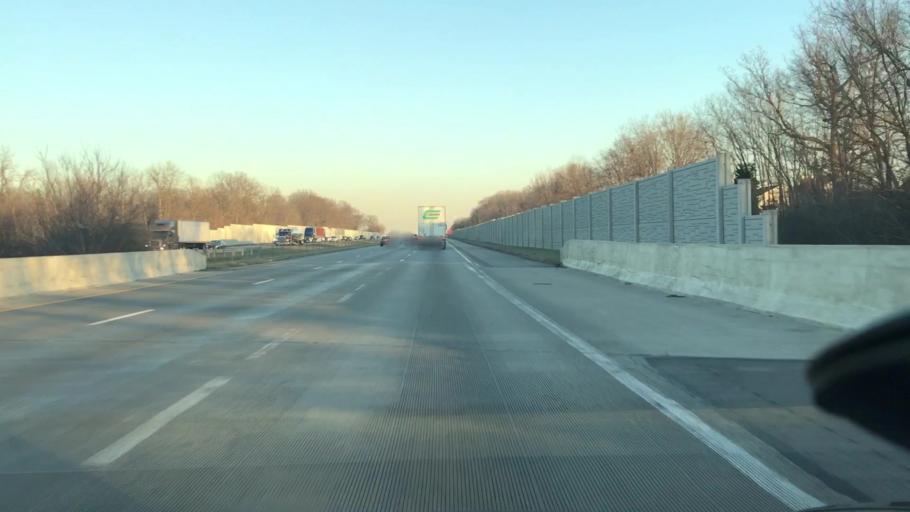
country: US
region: Ohio
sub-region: Franklin County
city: Lincoln Village
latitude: 39.9780
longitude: -83.1709
